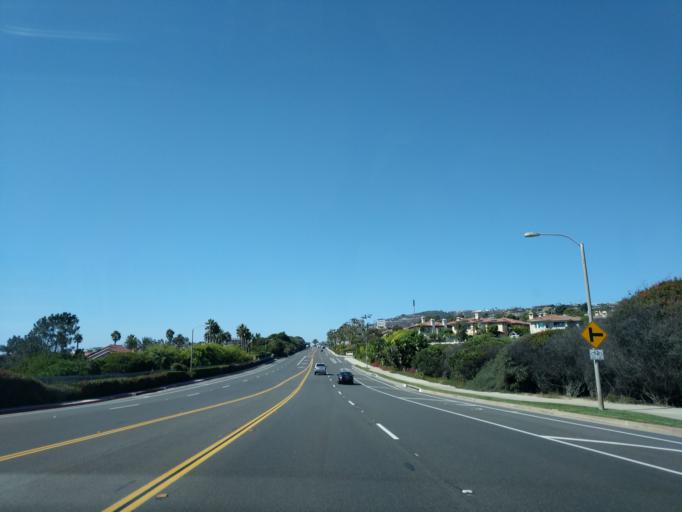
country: US
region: California
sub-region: Orange County
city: Dana Point
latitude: 33.4819
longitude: -117.7213
